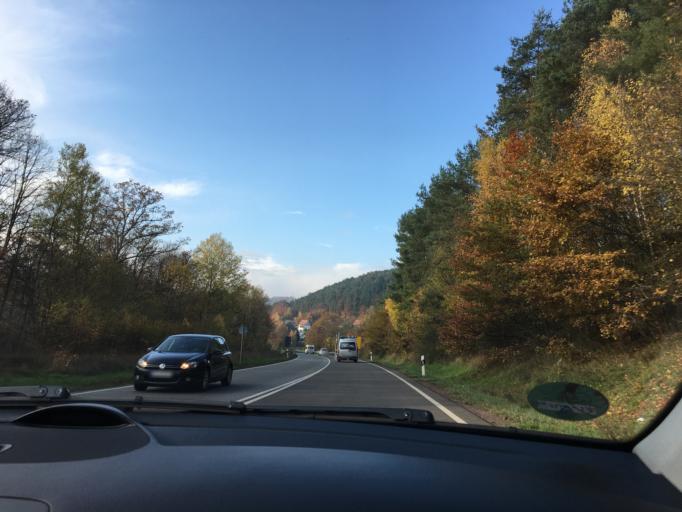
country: DE
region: Rheinland-Pfalz
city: Steinalben
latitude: 49.3140
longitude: 7.6655
